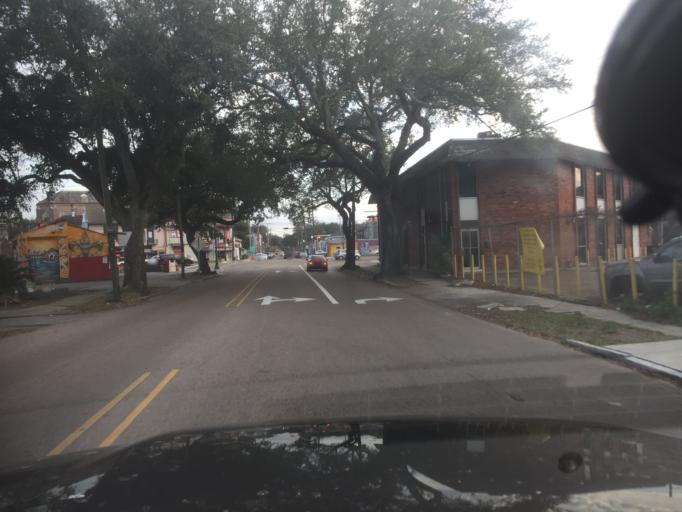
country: US
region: Louisiana
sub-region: Orleans Parish
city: New Orleans
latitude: 29.9781
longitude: -90.0775
